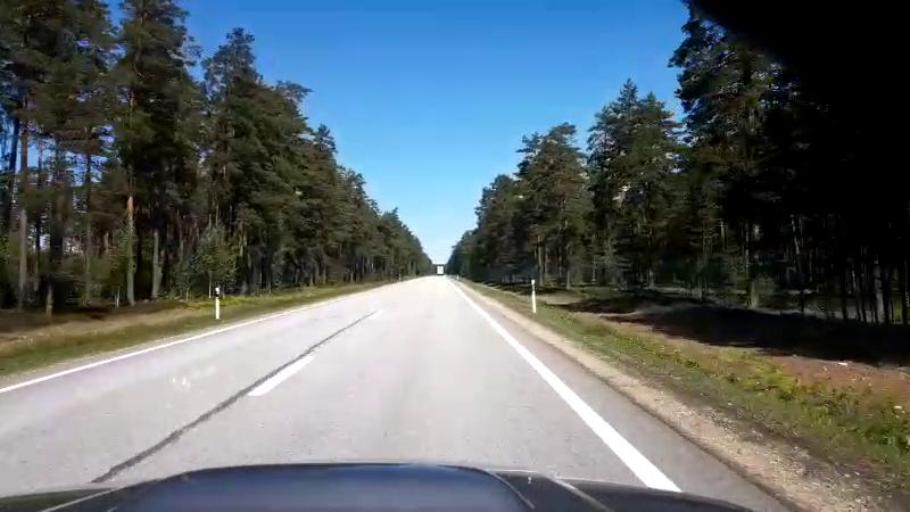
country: LV
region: Salacgrivas
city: Salacgriva
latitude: 57.5604
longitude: 24.4338
